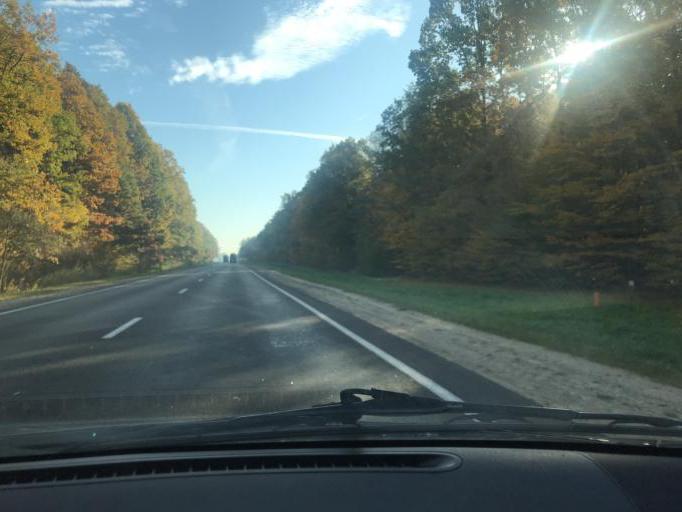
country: BY
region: Brest
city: Ivanava
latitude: 52.1526
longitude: 25.3639
